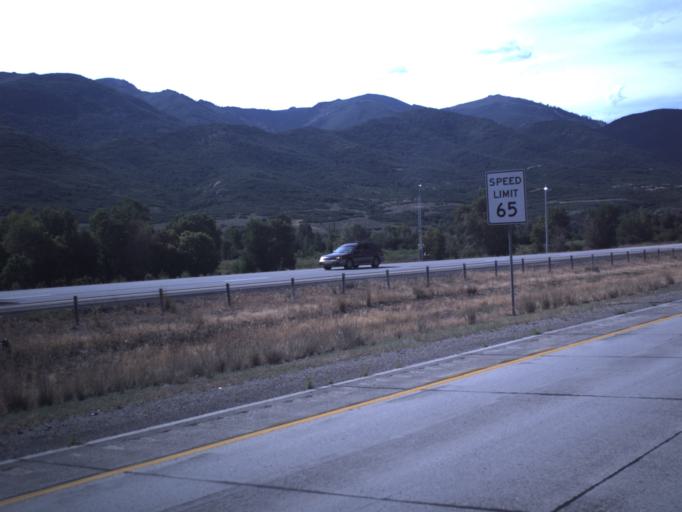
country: US
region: Utah
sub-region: Wasatch County
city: Heber
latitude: 40.5630
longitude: -111.4280
